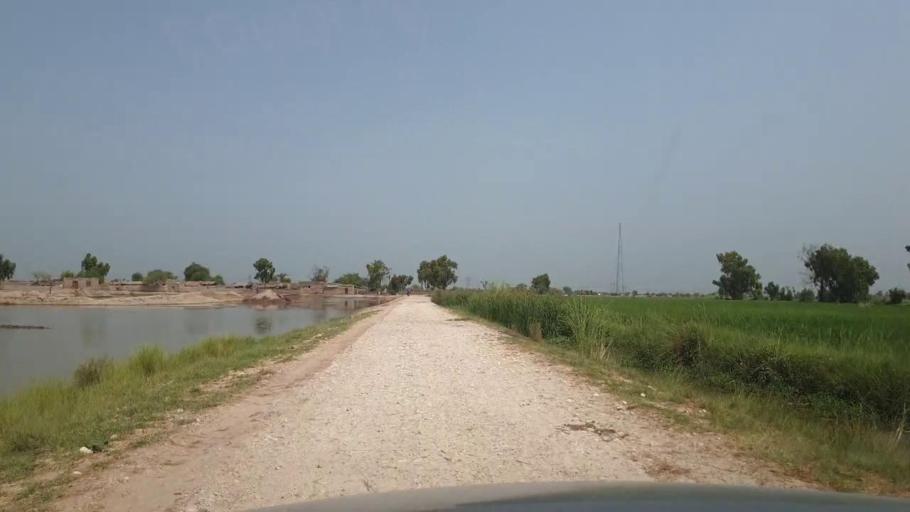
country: PK
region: Sindh
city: Madeji
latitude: 27.7990
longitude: 68.5322
